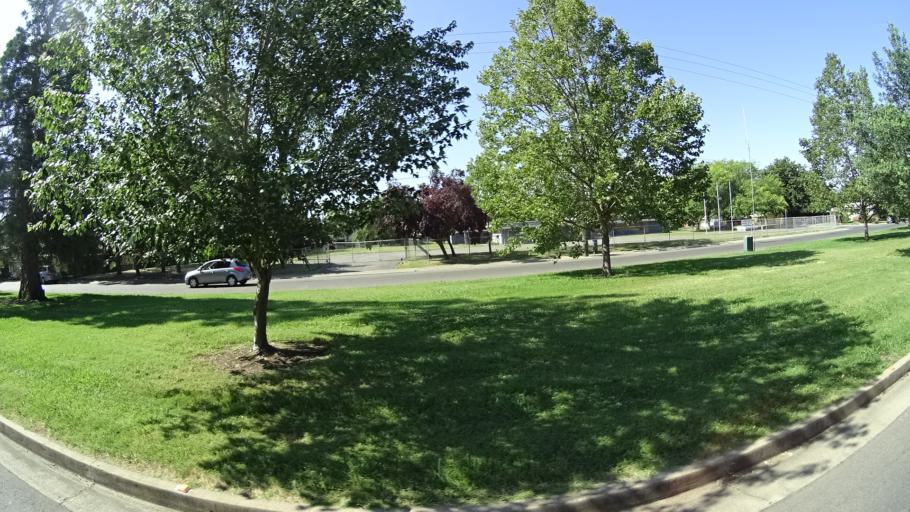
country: US
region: California
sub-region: Sacramento County
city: Florin
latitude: 38.5323
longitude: -121.4305
